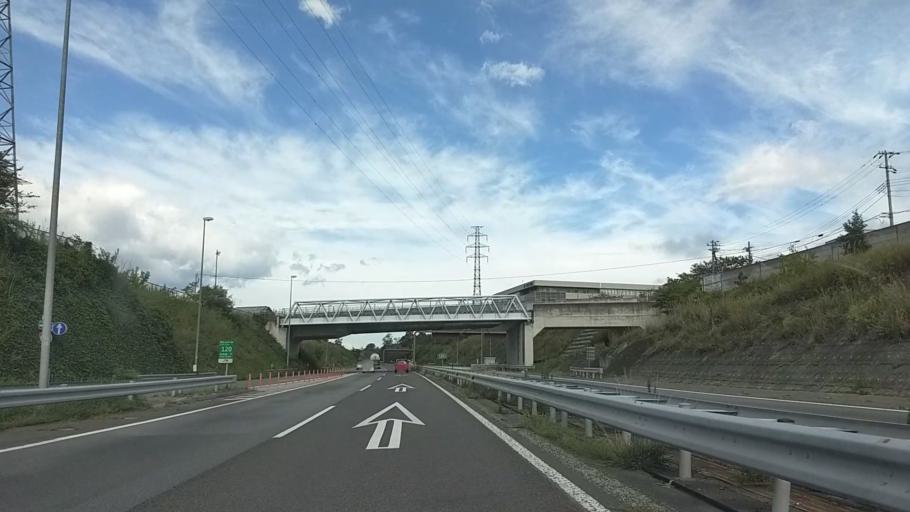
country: JP
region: Yamanashi
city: Ryuo
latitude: 35.6905
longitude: 138.4960
